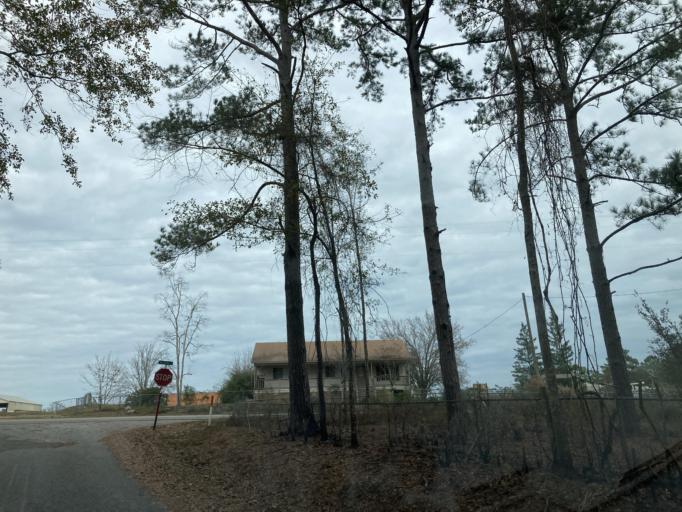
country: US
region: Mississippi
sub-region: Lamar County
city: Purvis
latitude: 31.0651
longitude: -89.2065
